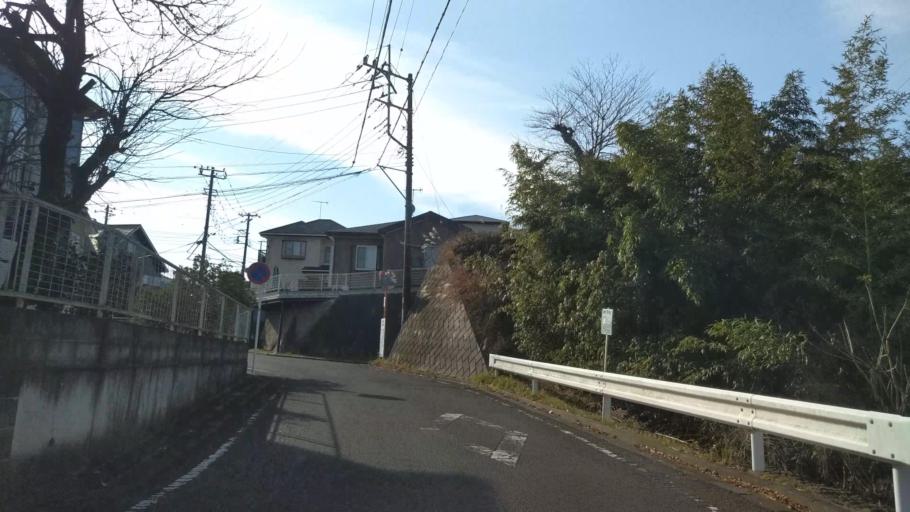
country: JP
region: Kanagawa
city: Hadano
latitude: 35.3811
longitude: 139.2421
